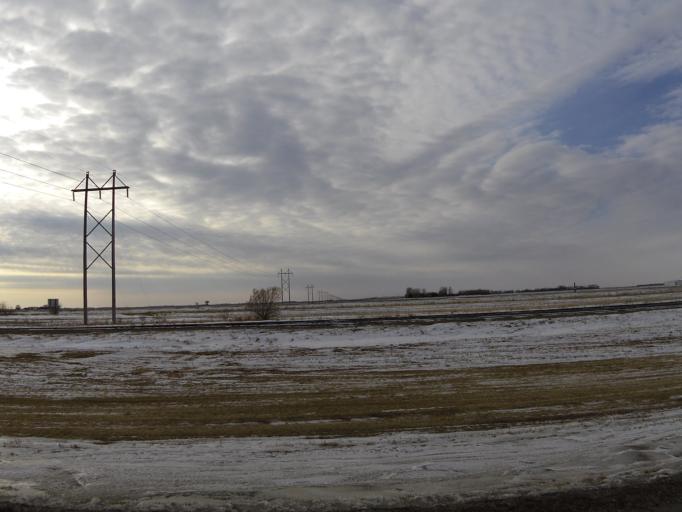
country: US
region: North Dakota
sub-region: Walsh County
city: Grafton
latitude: 48.5849
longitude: -97.1788
